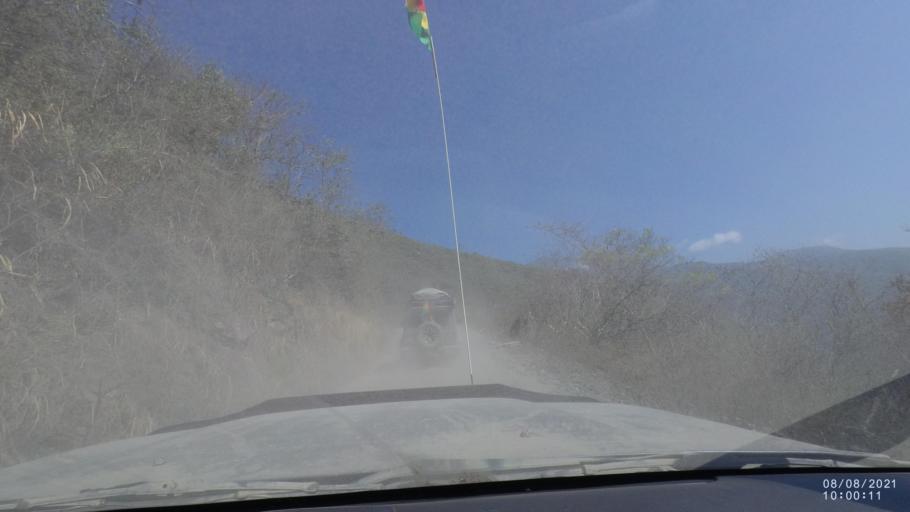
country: BO
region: La Paz
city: Quime
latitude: -16.6463
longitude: -66.7253
